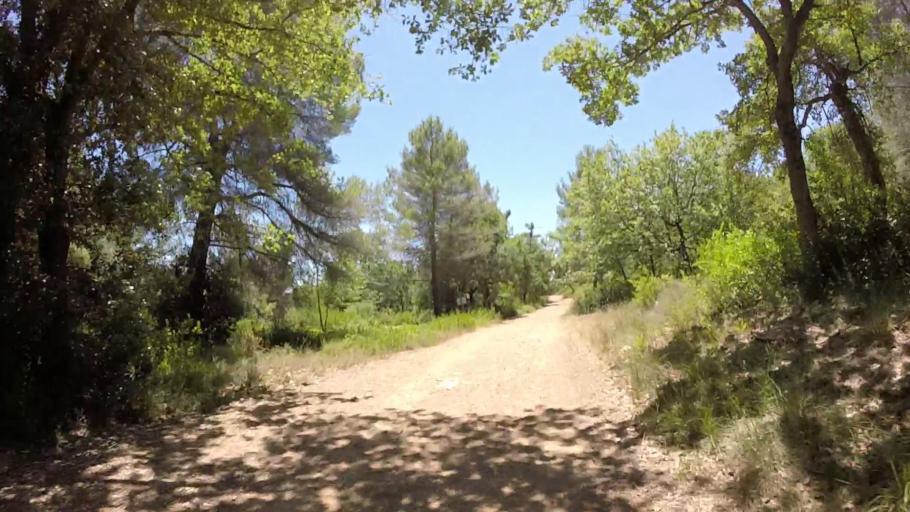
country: FR
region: Provence-Alpes-Cote d'Azur
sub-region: Departement des Alpes-Maritimes
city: Valbonne
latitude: 43.6337
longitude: 7.0335
